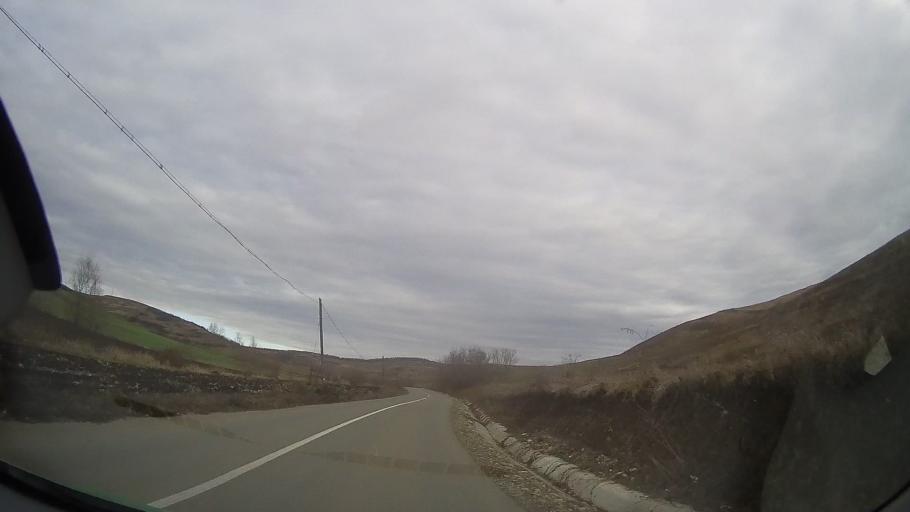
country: RO
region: Bistrita-Nasaud
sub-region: Comuna Silvasu de Campie
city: Silvasu de Campie
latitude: 46.8192
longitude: 24.2971
